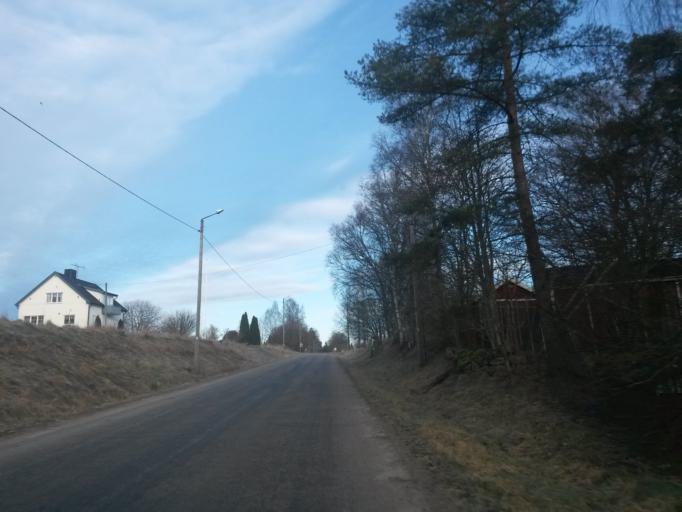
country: SE
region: Vaestra Goetaland
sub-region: Boras Kommun
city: Boras
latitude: 57.8599
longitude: 12.9284
